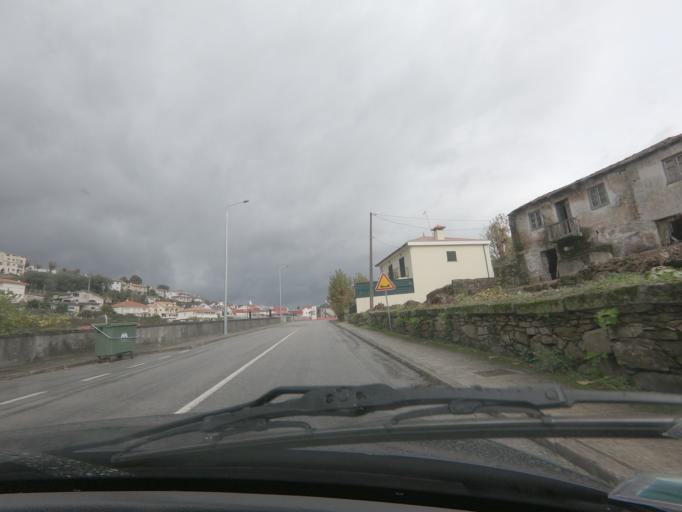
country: PT
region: Vila Real
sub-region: Mondim de Basto
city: Mondim de Basto
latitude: 41.4052
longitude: -7.9571
